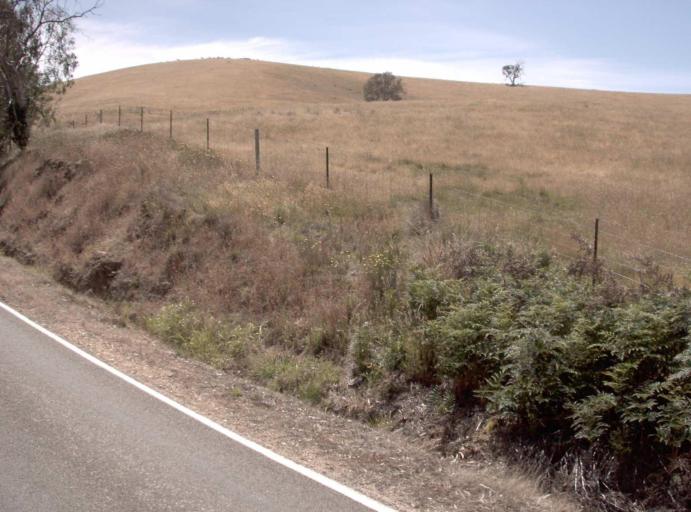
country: AU
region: Victoria
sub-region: Alpine
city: Mount Beauty
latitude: -37.0510
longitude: 147.6181
